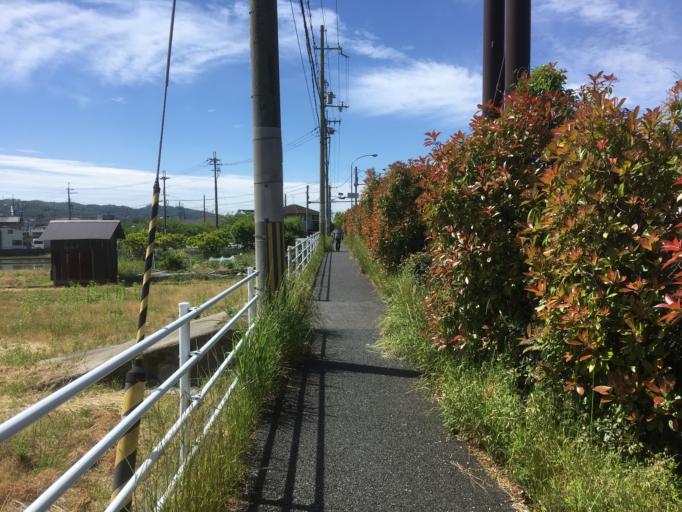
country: JP
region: Nara
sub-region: Ikoma-shi
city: Ikoma
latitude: 34.6790
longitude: 135.7063
